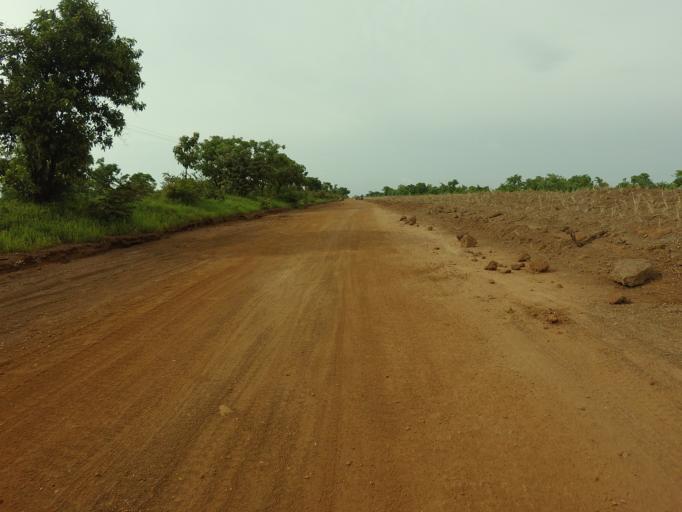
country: GH
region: Northern
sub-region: Yendi
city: Yendi
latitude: 9.6509
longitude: -0.0702
